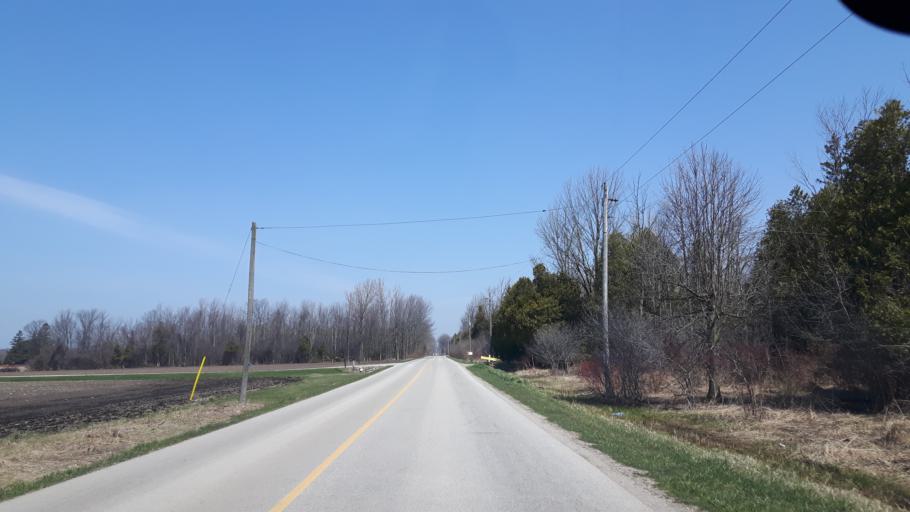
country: CA
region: Ontario
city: Goderich
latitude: 43.6853
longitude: -81.6847
